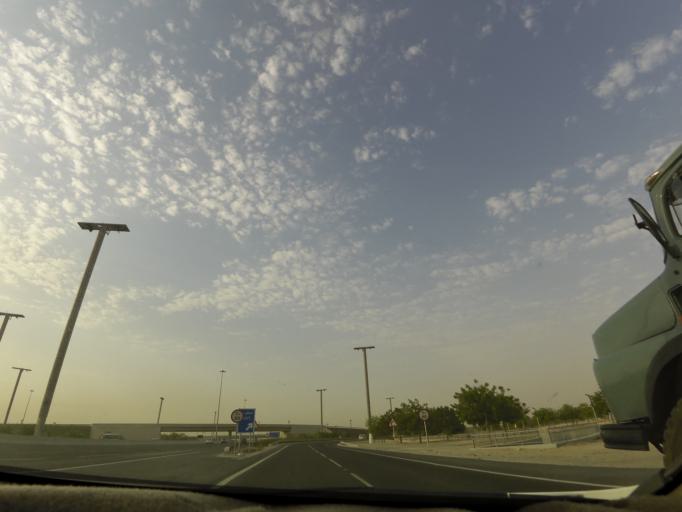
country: QA
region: Al Wakrah
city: Al Wakrah
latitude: 25.2438
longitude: 51.5894
